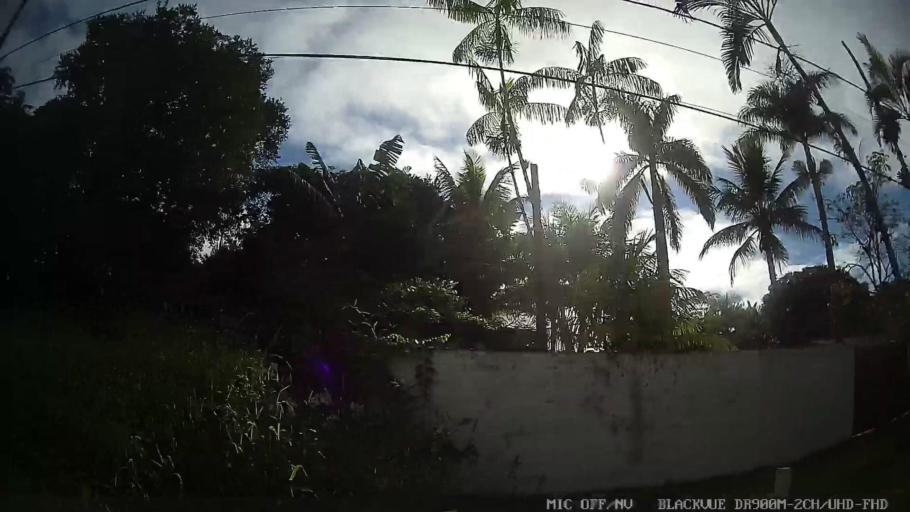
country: BR
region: Sao Paulo
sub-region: Peruibe
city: Peruibe
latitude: -24.2326
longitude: -46.9137
